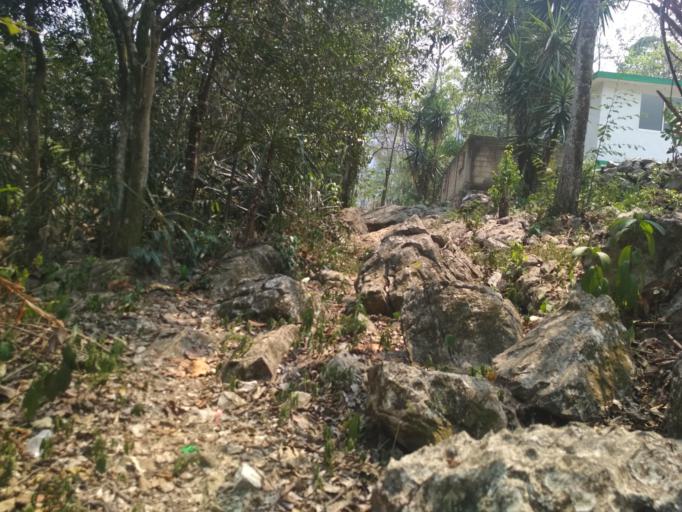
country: MX
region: Veracruz
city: Cosolapa
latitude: 18.5945
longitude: -96.7281
